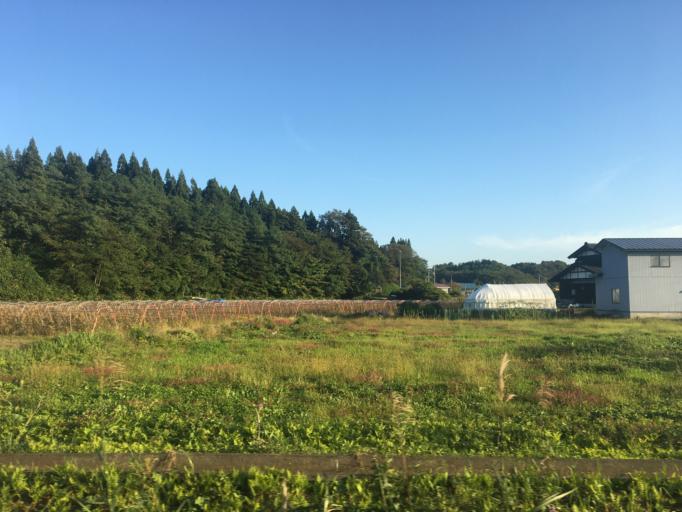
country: JP
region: Akita
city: Takanosu
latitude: 40.2054
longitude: 140.3508
